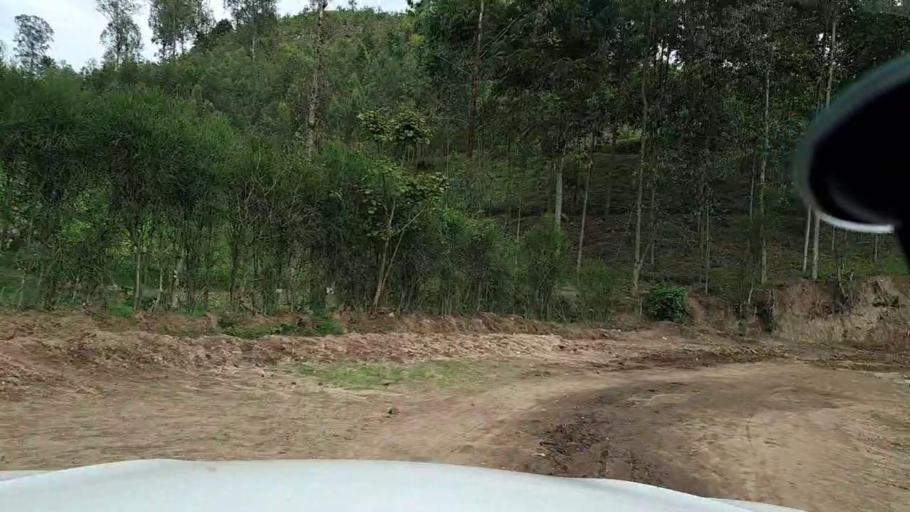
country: RW
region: Southern Province
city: Gitarama
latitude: -2.1275
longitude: 29.6602
